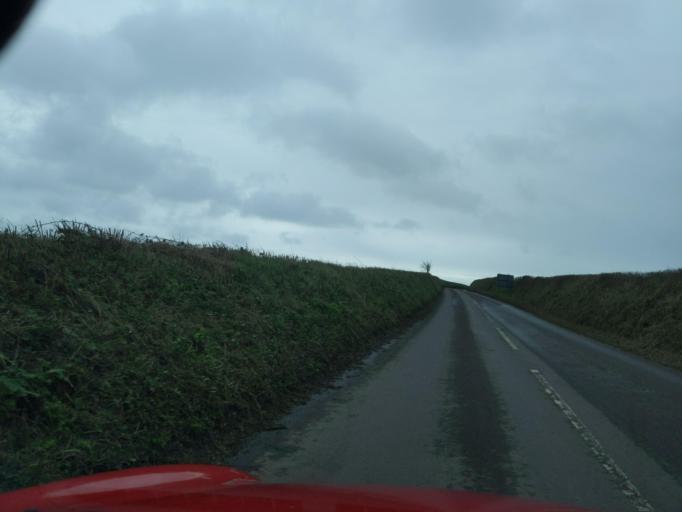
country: GB
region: England
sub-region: Devon
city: Modbury
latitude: 50.3256
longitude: -3.8859
